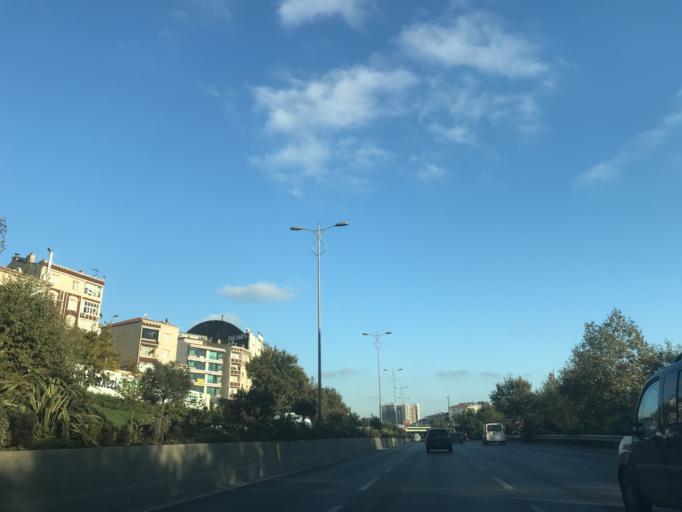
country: TR
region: Istanbul
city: Esenler
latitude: 41.0495
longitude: 28.8741
